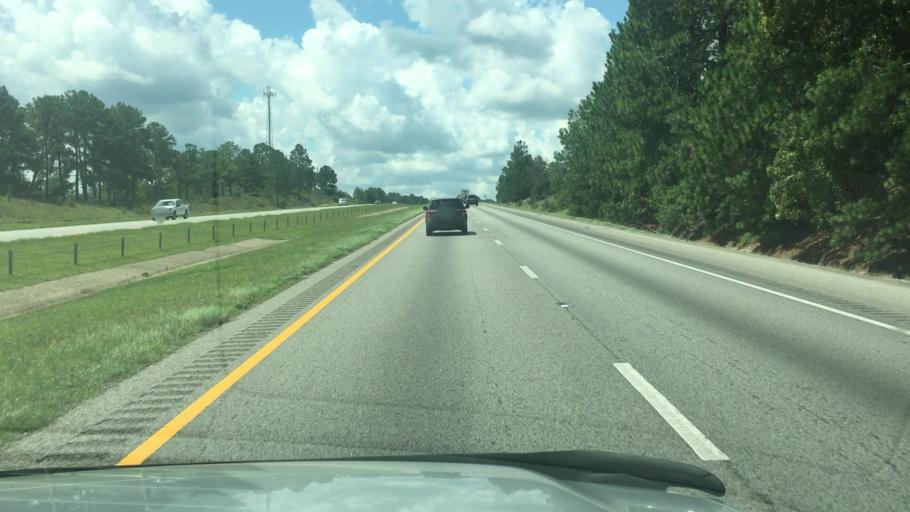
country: US
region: South Carolina
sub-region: Kershaw County
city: Lugoff
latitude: 34.1739
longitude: -80.7079
